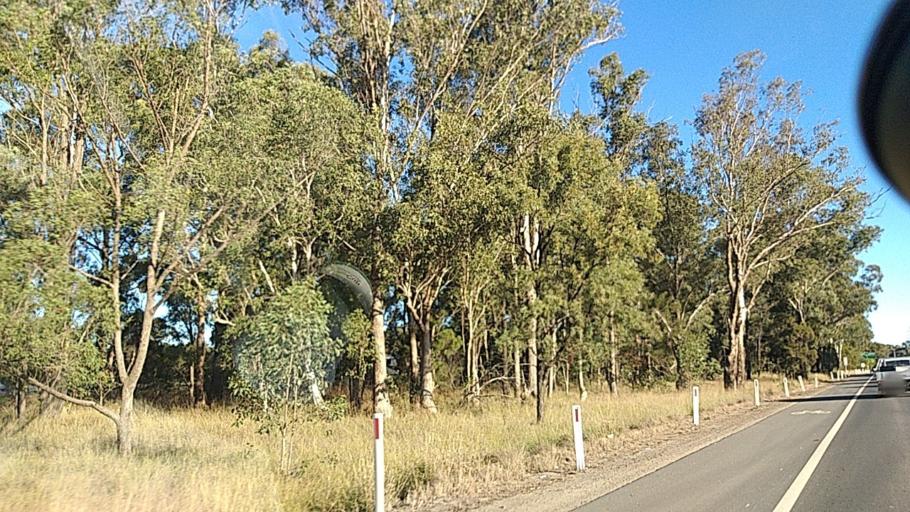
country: AU
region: New South Wales
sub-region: Hawkesbury
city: South Windsor
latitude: -33.6361
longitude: 150.7872
